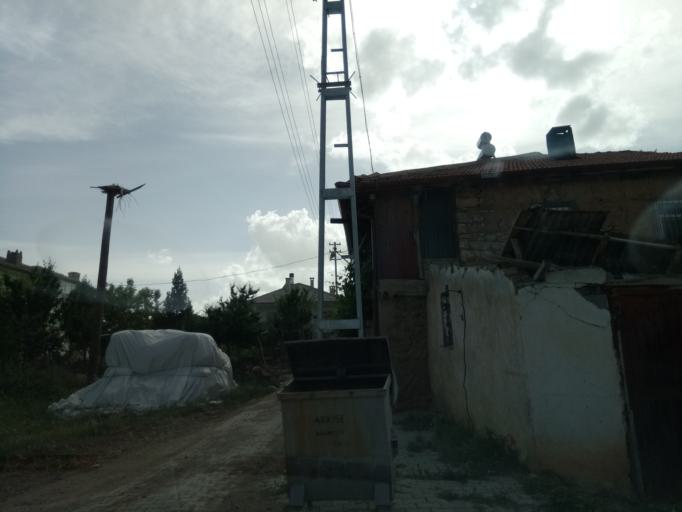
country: TR
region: Konya
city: Ahirli
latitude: 37.2871
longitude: 32.1791
